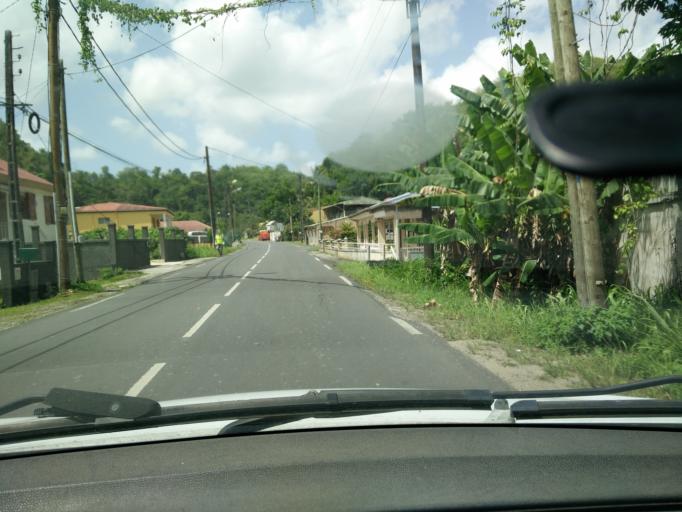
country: GP
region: Guadeloupe
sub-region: Guadeloupe
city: Les Abymes
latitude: 16.2952
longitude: -61.4622
